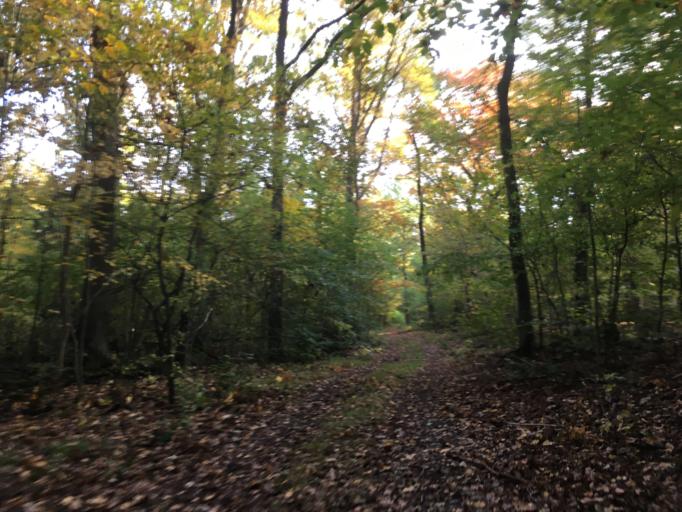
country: DE
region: Berlin
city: Buch
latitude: 52.6553
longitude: 13.4845
